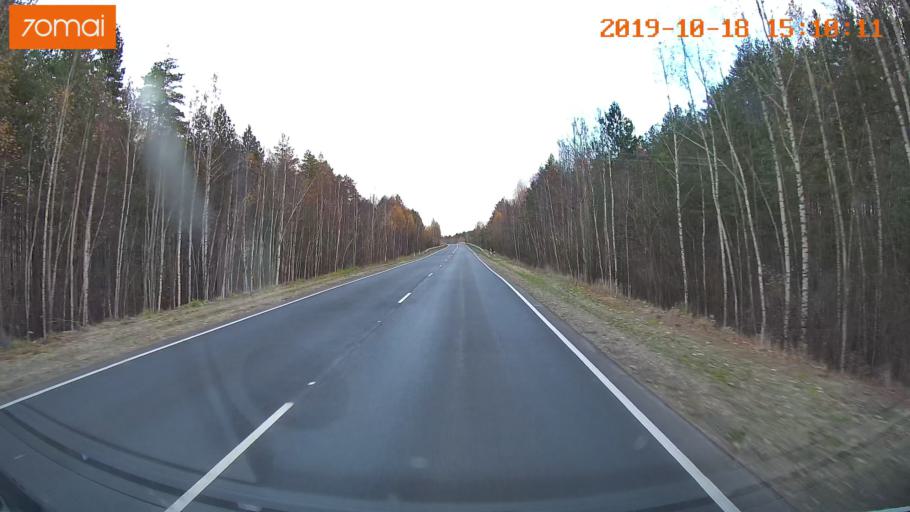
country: RU
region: Vladimir
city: Gus'-Khrustal'nyy
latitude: 55.5677
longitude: 40.6369
